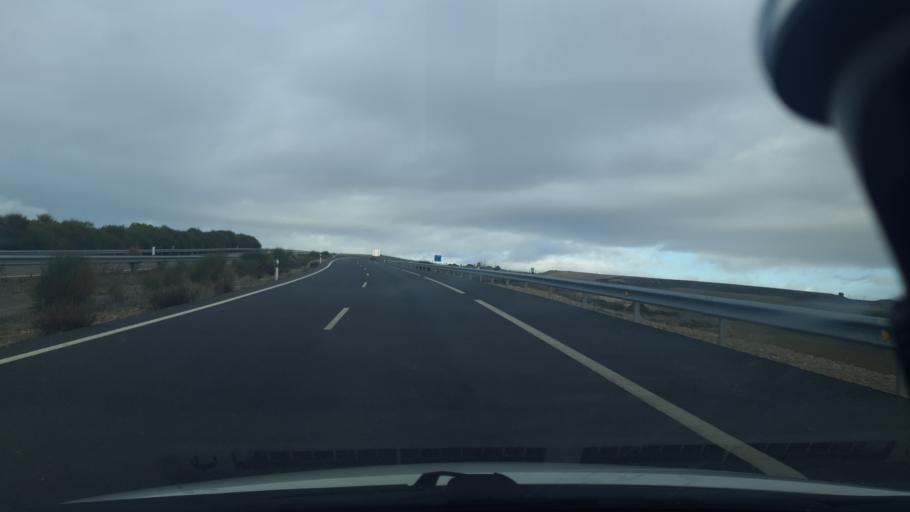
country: ES
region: Castille and Leon
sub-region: Provincia de Segovia
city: Cuellar
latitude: 41.3949
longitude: -4.2917
